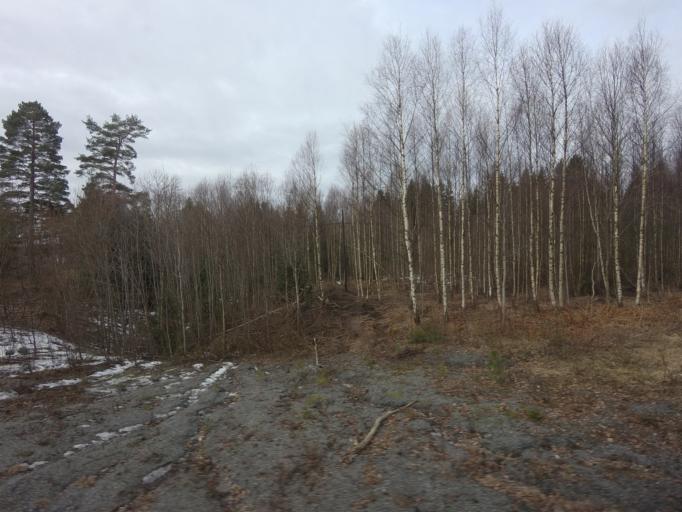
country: NO
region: Akershus
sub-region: Enebakk
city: Flateby
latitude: 59.8074
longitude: 11.2531
